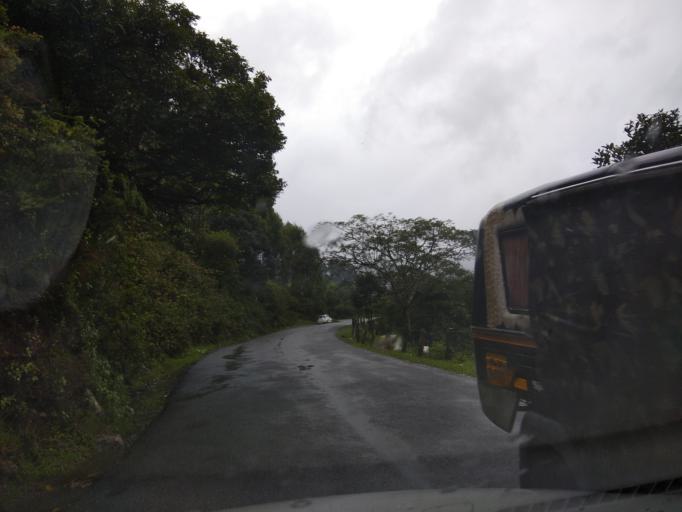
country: IN
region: Kerala
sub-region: Idukki
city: Munnar
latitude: 10.1381
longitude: 77.0619
